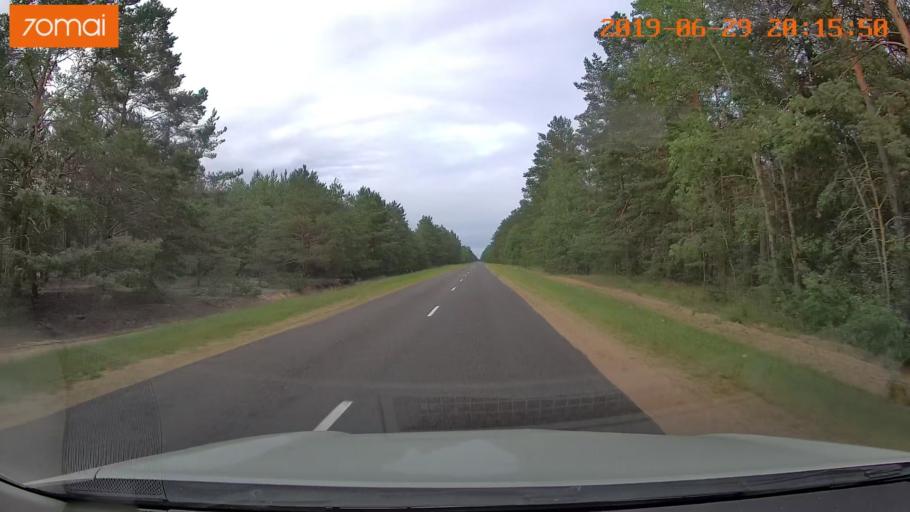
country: BY
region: Brest
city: Asnyezhytsy
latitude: 52.3770
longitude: 26.1838
